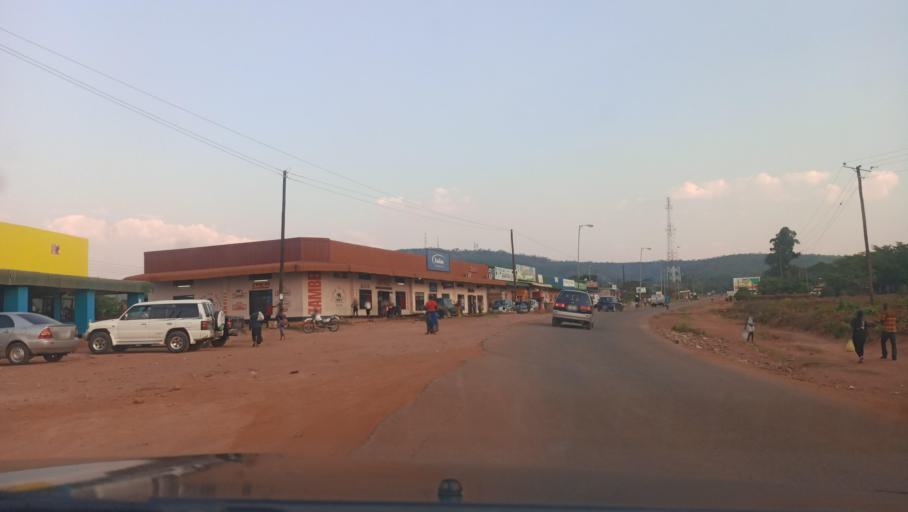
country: ZM
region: Northern
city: Mpika
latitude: -11.8365
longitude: 31.4474
